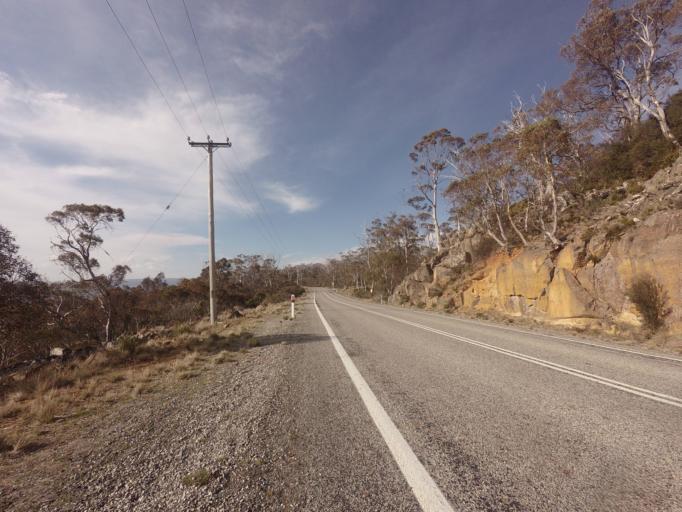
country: AU
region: Tasmania
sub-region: Meander Valley
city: Deloraine
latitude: -41.9846
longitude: 146.7144
